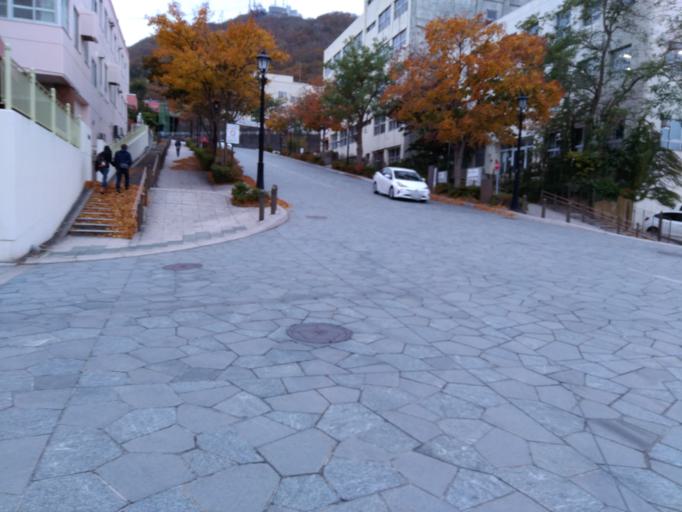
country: JP
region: Hokkaido
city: Hakodate
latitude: 41.7644
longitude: 140.7125
